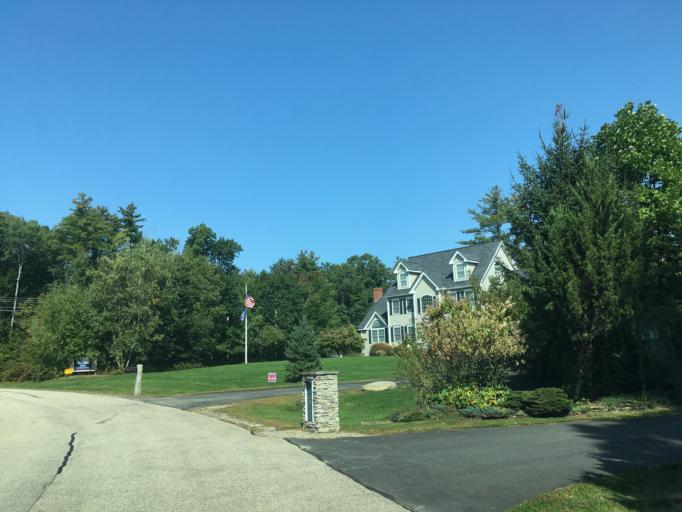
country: US
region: New Hampshire
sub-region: Rockingham County
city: Stratham Station
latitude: 43.0060
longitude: -70.8879
